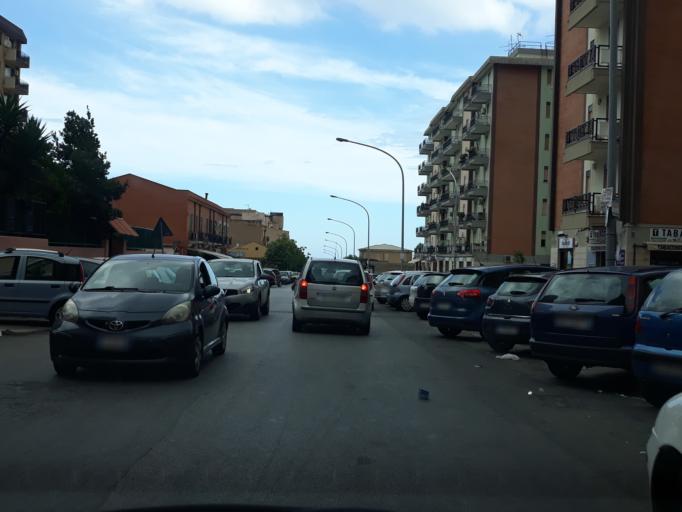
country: IT
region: Sicily
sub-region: Palermo
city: Ciaculli
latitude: 38.1006
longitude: 13.3932
